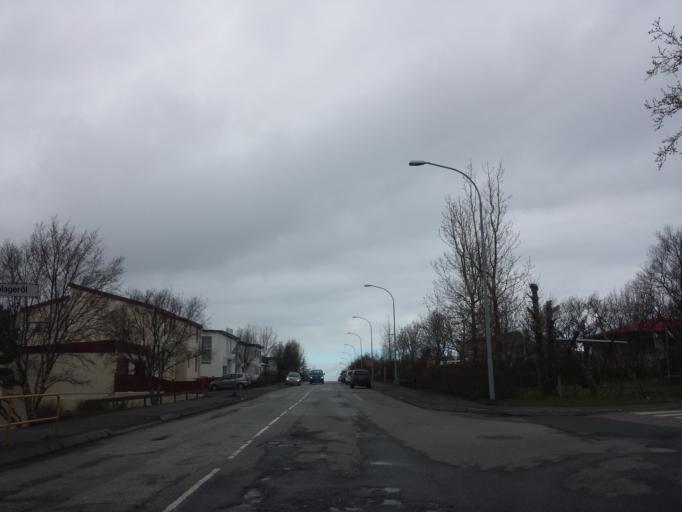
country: IS
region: Capital Region
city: Kopavogur
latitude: 64.1112
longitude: -21.9227
